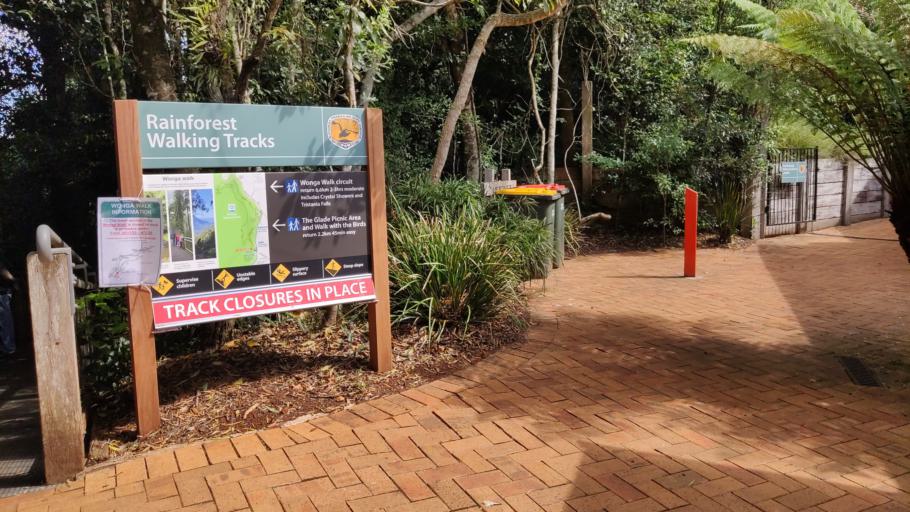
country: AU
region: New South Wales
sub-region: Bellingen
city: Dorrigo
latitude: -30.3638
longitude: 152.7291
